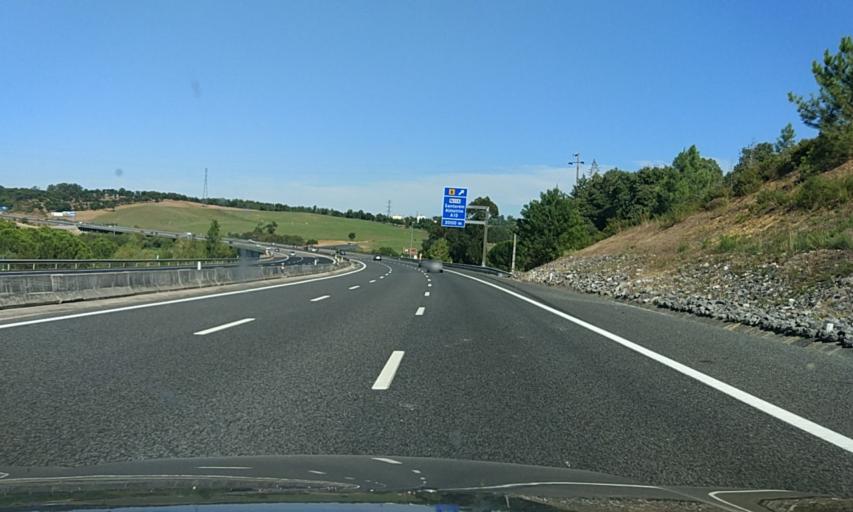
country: PT
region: Santarem
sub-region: Santarem
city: Santarem
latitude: 39.2395
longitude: -8.7503
